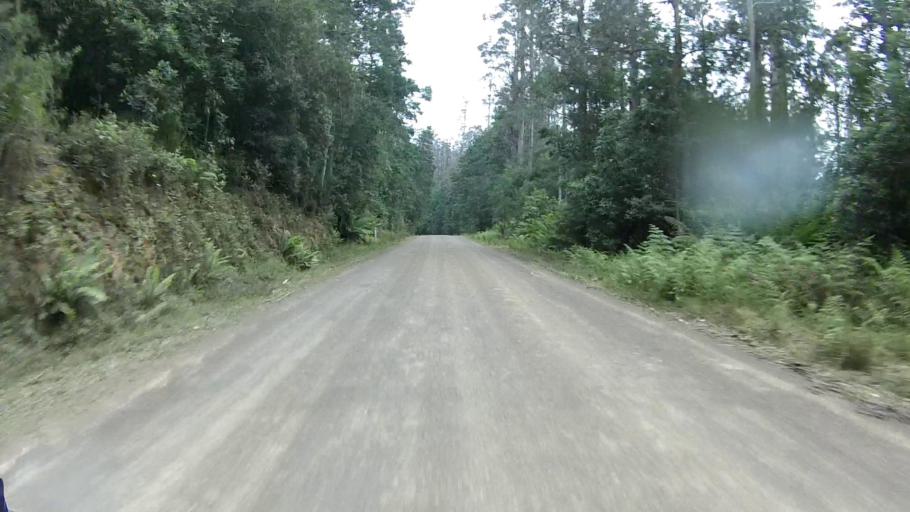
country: AU
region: Tasmania
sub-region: Sorell
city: Sorell
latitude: -42.7112
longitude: 147.8401
